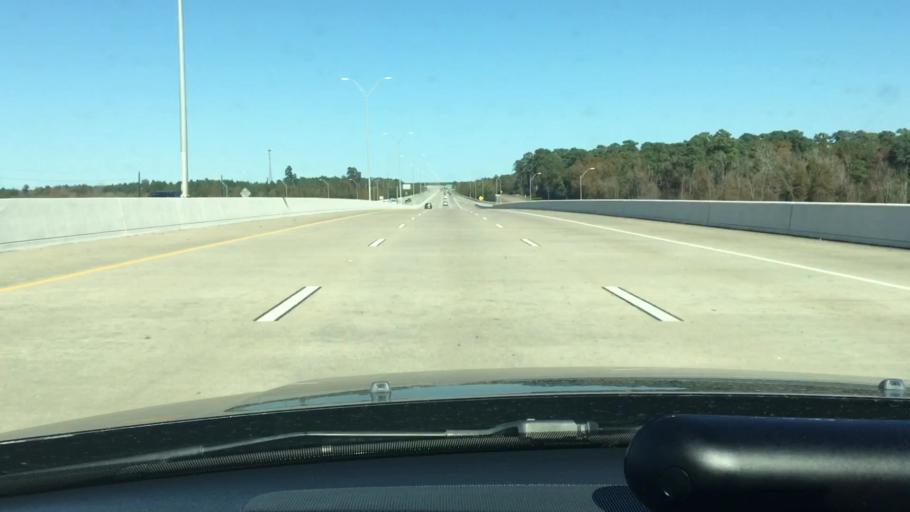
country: US
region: Texas
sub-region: Harris County
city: Sheldon
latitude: 29.8540
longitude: -95.1869
